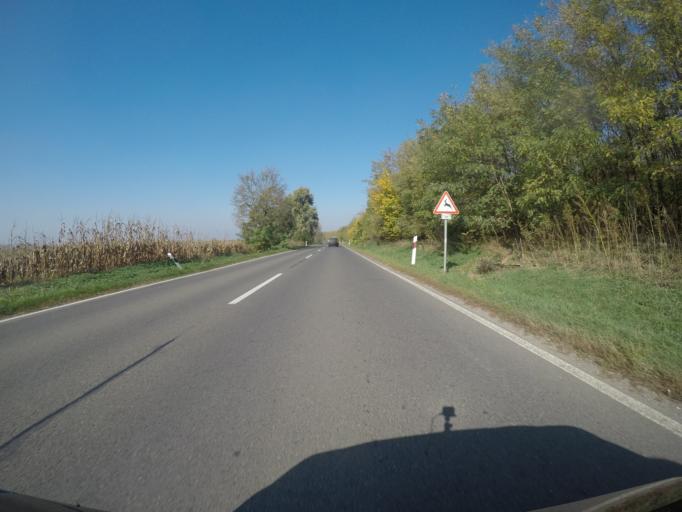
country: HU
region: Tolna
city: Szedres
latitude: 46.4884
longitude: 18.6793
